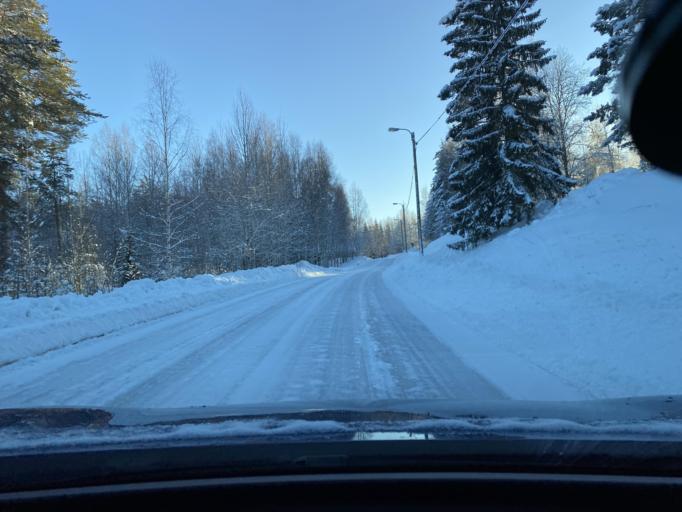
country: FI
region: Southern Savonia
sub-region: Mikkeli
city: Kangasniemi
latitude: 62.0085
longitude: 26.6215
